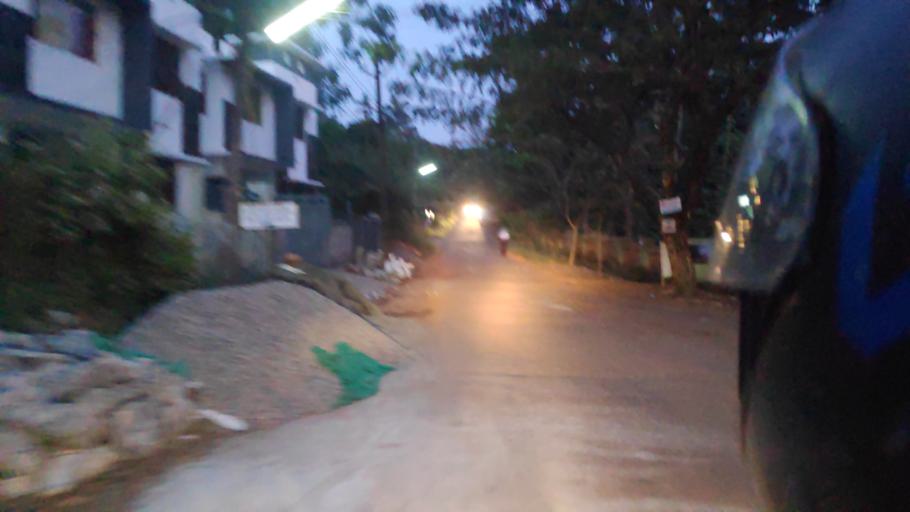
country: IN
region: Kerala
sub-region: Kozhikode
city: Kunnamangalam
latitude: 11.2801
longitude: 75.8337
